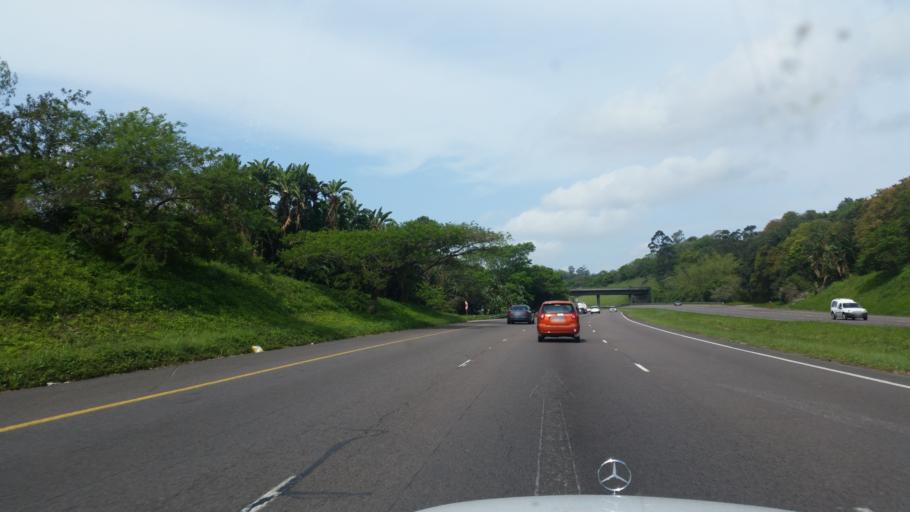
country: ZA
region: KwaZulu-Natal
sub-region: eThekwini Metropolitan Municipality
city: Berea
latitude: -29.8337
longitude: 30.8848
